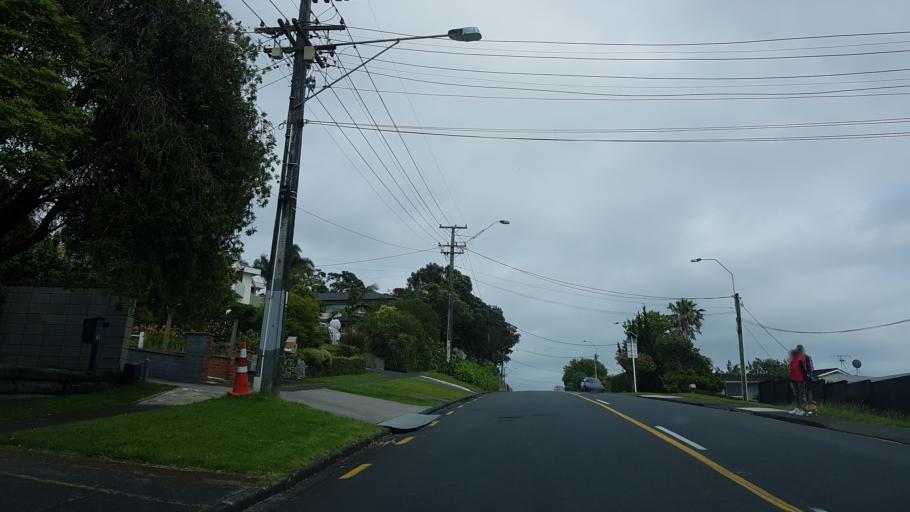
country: NZ
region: Auckland
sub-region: Auckland
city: North Shore
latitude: -36.8046
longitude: 174.7500
